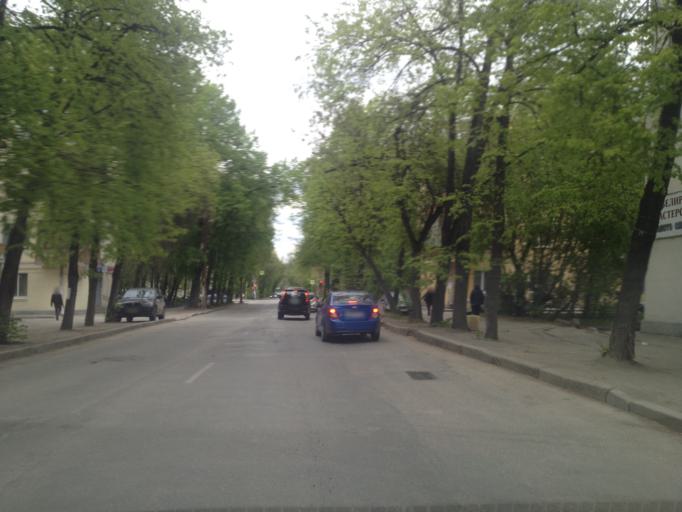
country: RU
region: Sverdlovsk
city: Yekaterinburg
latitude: 56.8891
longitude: 60.5971
